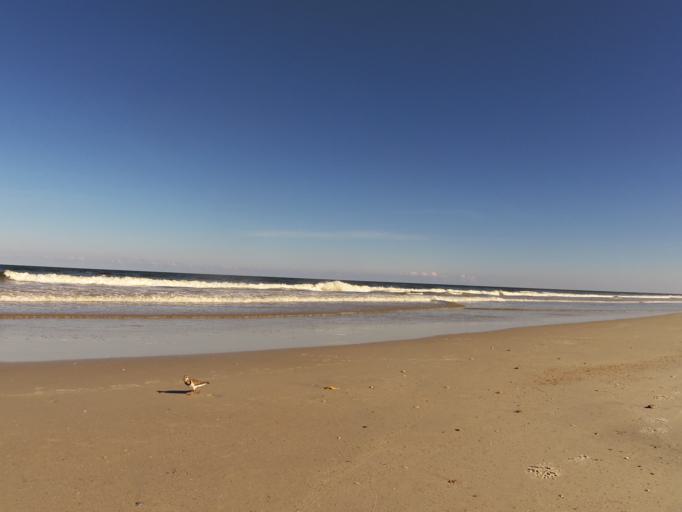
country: US
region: Florida
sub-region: Saint Johns County
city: Sawgrass
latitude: 30.1783
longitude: -81.3599
